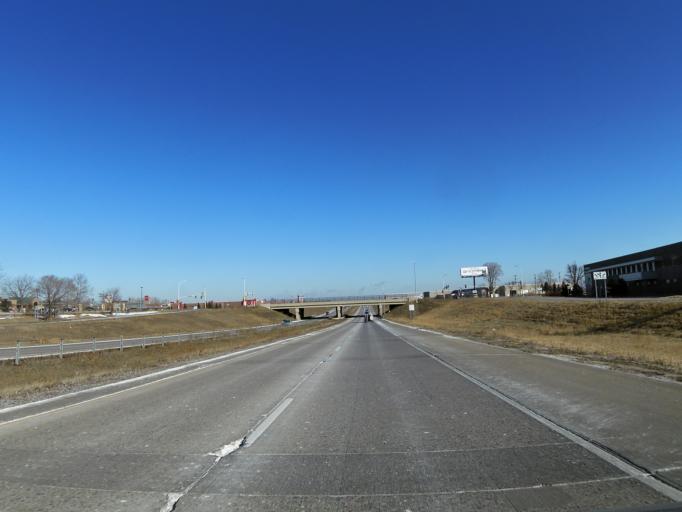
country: US
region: Minnesota
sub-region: Hennepin County
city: Richfield
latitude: 44.8815
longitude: -93.2468
